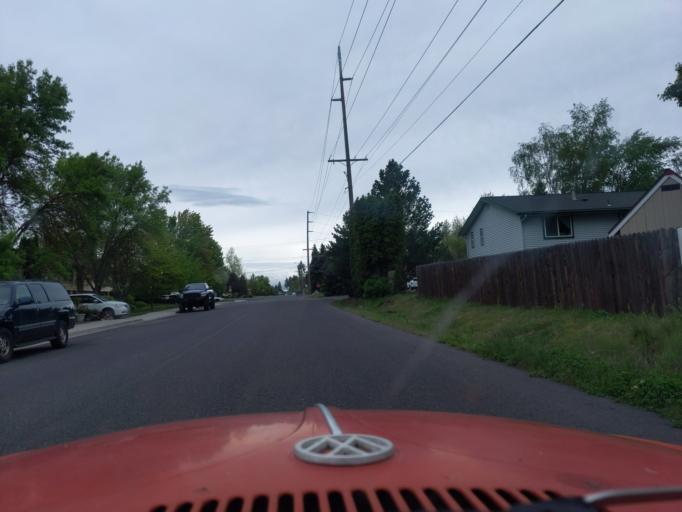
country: US
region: Washington
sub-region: Spokane County
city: Spokane
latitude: 47.6033
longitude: -117.3792
